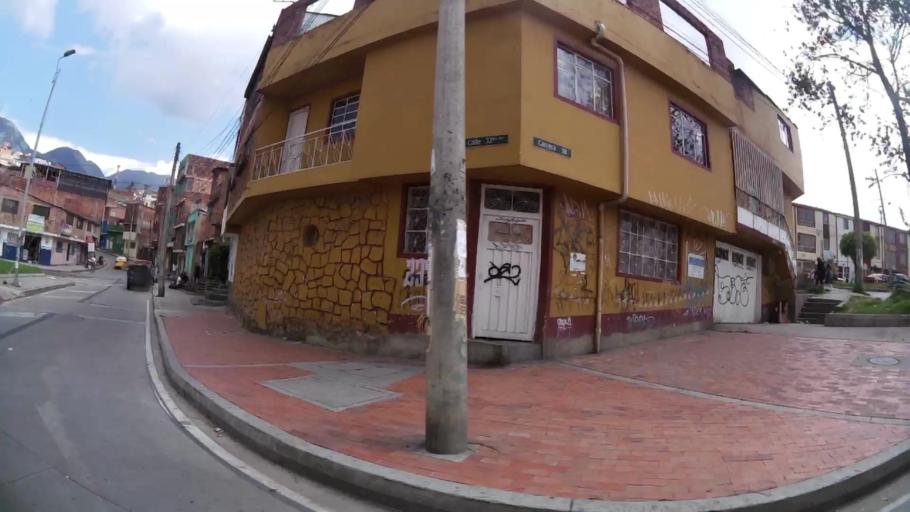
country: CO
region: Bogota D.C.
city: Bogota
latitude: 4.5620
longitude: -74.0967
